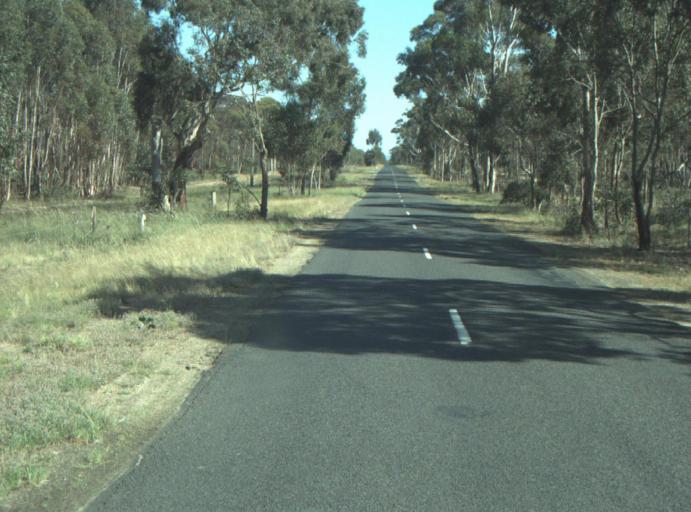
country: AU
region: Victoria
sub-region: Greater Geelong
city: Lara
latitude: -37.9620
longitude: 144.4038
